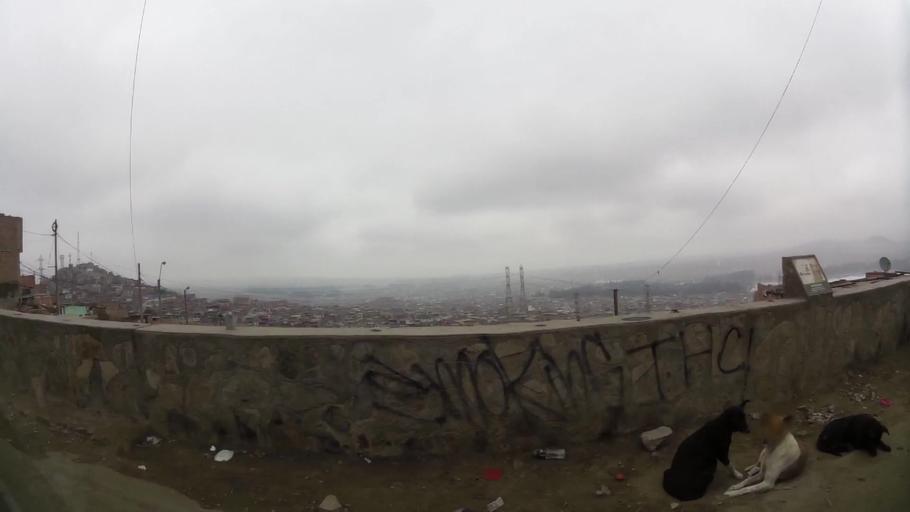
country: PE
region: Lima
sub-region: Lima
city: Surco
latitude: -12.1798
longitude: -76.9550
